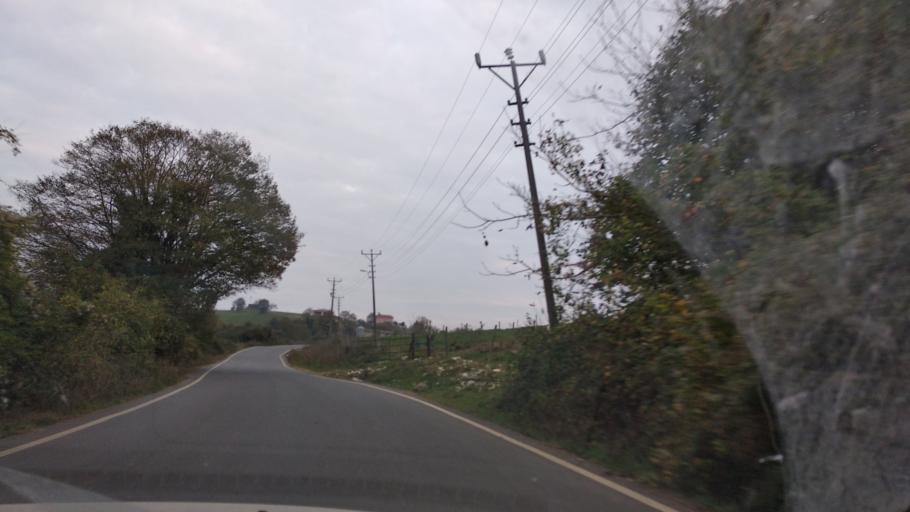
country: TR
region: Sakarya
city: Ortakoy
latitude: 41.0352
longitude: 30.6581
